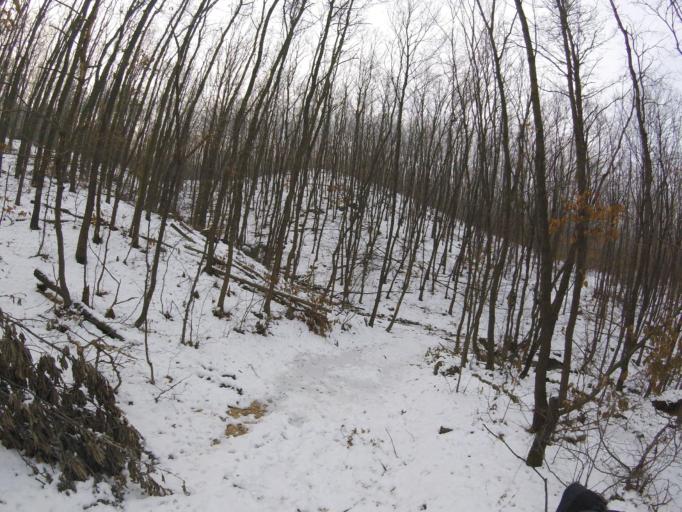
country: HU
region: Heves
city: Sirok
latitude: 47.9089
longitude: 20.1646
